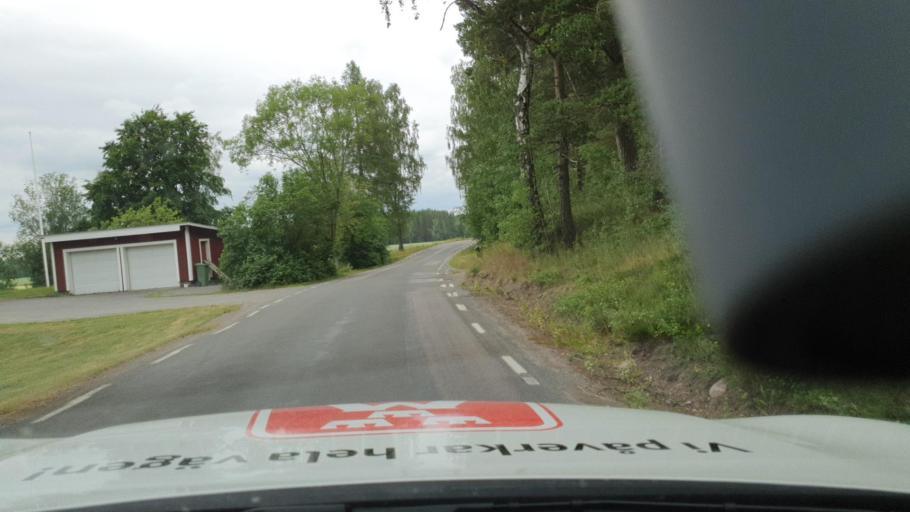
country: SE
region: Vaestra Goetaland
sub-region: Tidaholms Kommun
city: Olofstorp
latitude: 58.2408
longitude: 14.0955
